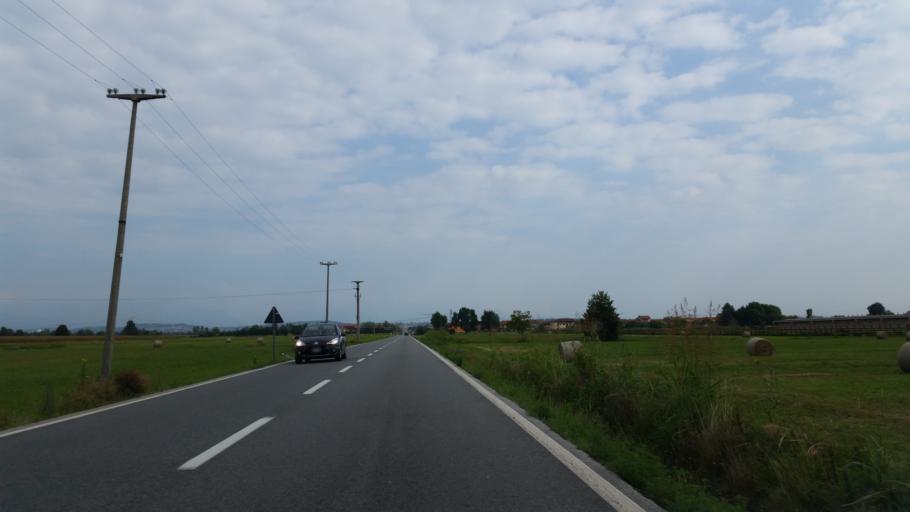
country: IT
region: Piedmont
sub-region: Provincia di Torino
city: Montanaro
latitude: 45.2487
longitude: 7.8916
